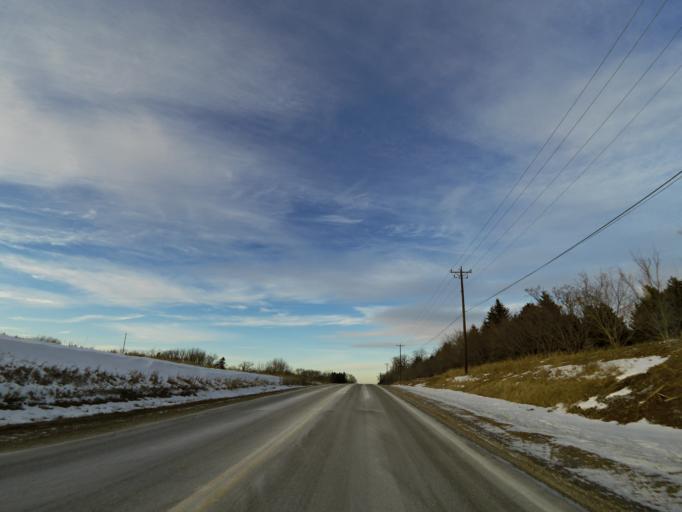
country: US
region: Minnesota
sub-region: Washington County
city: Afton
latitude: 44.8953
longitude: -92.8428
